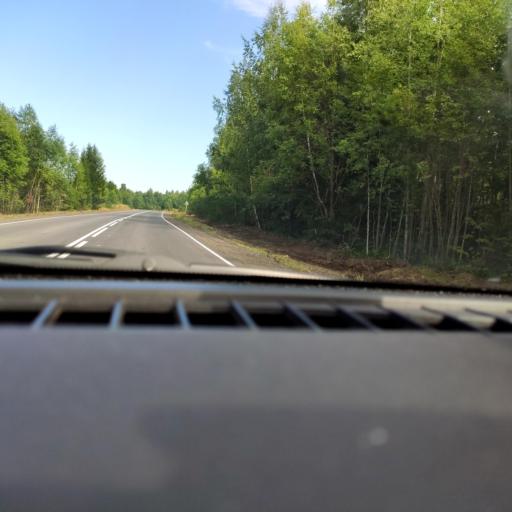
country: RU
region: Perm
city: Polazna
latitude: 58.3349
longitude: 56.1959
